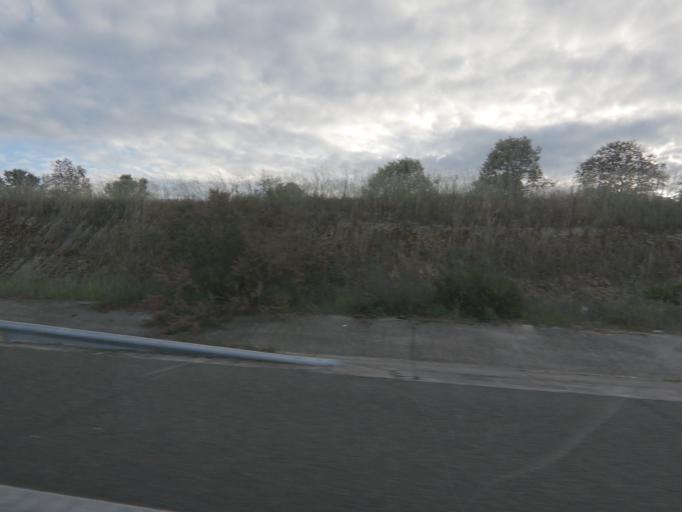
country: ES
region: Extremadura
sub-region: Provincia de Caceres
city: Caceres
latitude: 39.4803
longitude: -6.4354
